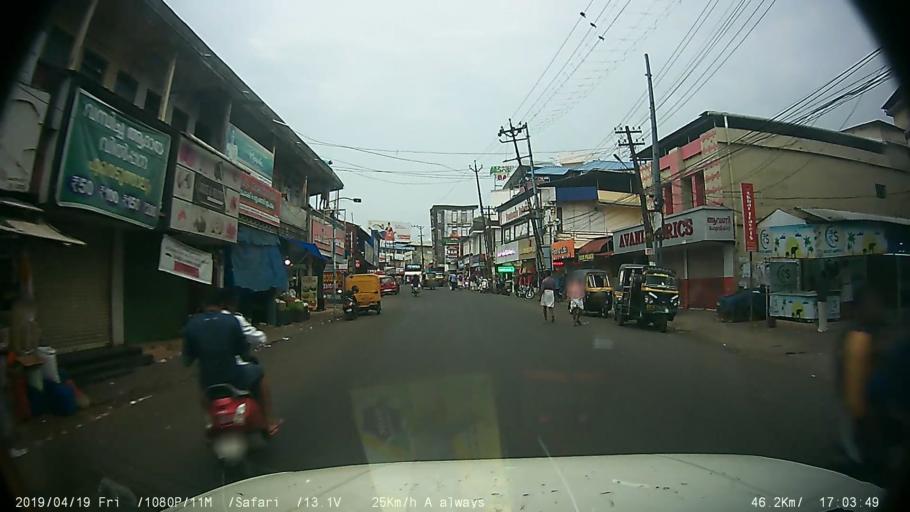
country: IN
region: Kerala
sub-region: Kottayam
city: Changanacheri
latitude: 9.4466
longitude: 76.5412
